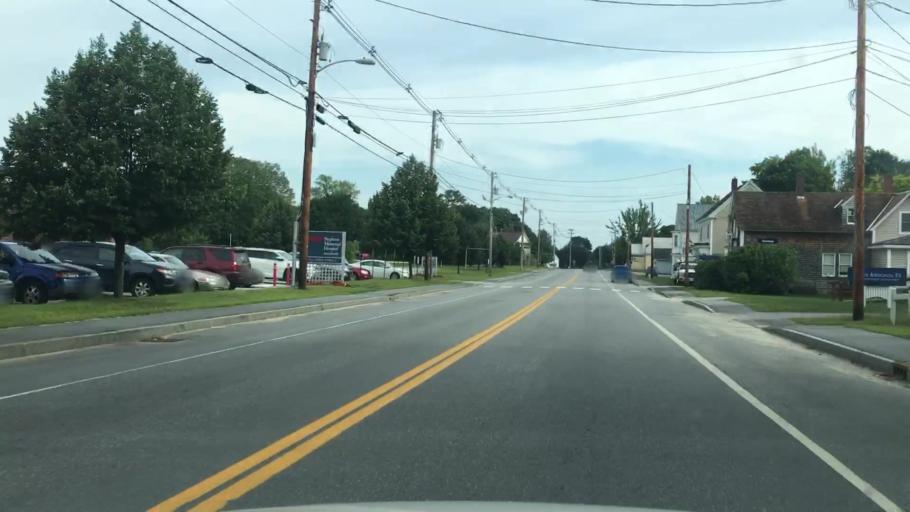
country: US
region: Maine
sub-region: Oxford County
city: Norway
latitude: 44.2098
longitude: -70.5332
